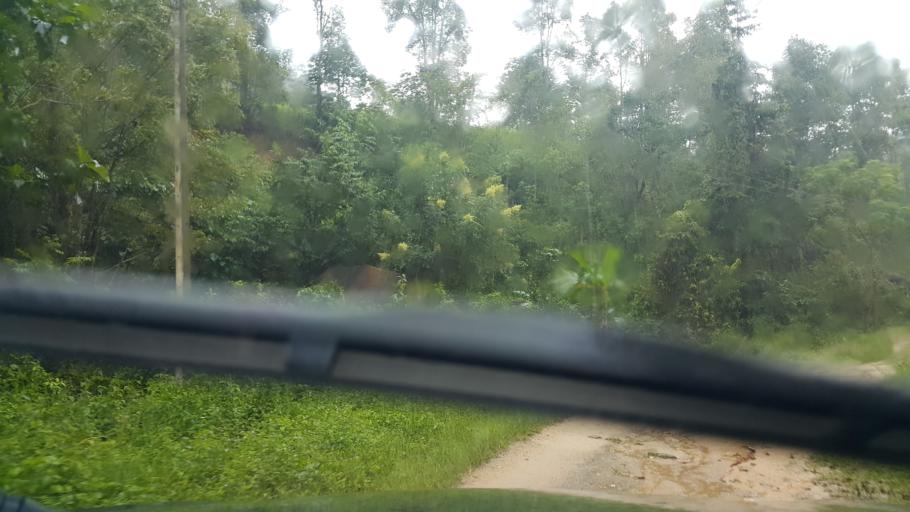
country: TH
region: Chiang Rai
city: Wiang Pa Pao
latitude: 19.1292
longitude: 99.3451
